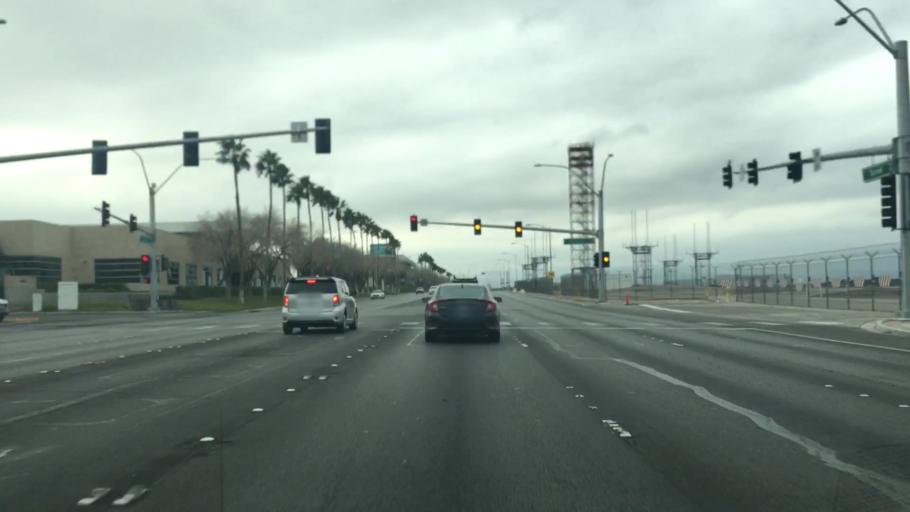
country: US
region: Nevada
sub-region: Clark County
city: Paradise
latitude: 36.0714
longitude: -115.1541
